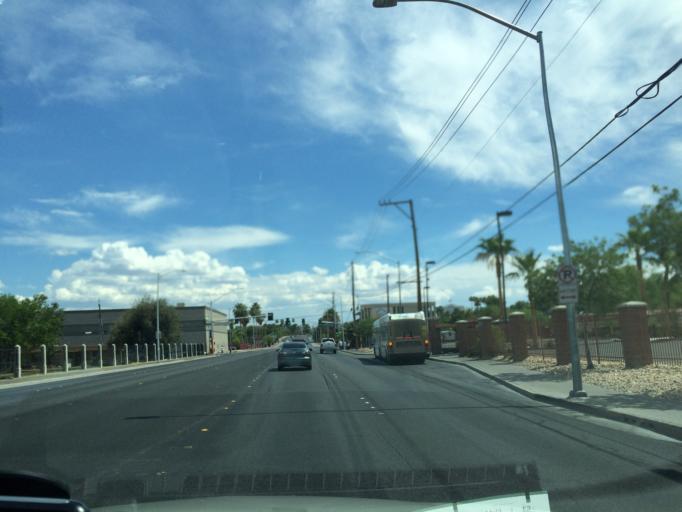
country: US
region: Nevada
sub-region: Clark County
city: Las Vegas
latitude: 36.1875
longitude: -115.1341
